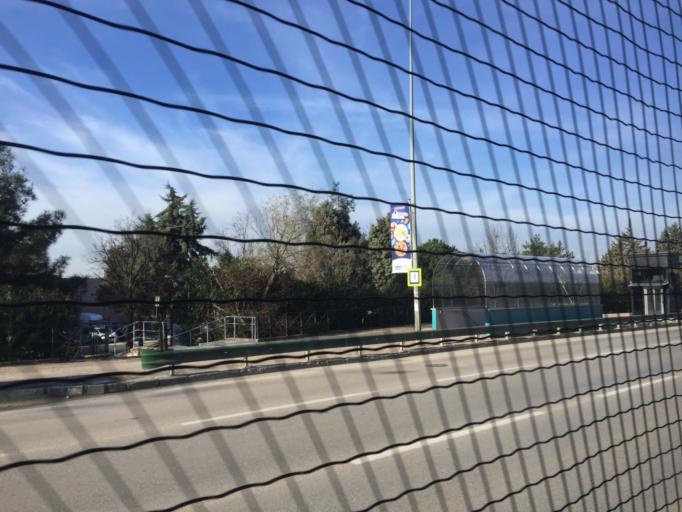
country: TR
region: Bursa
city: Niluefer
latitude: 40.2432
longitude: 28.9672
